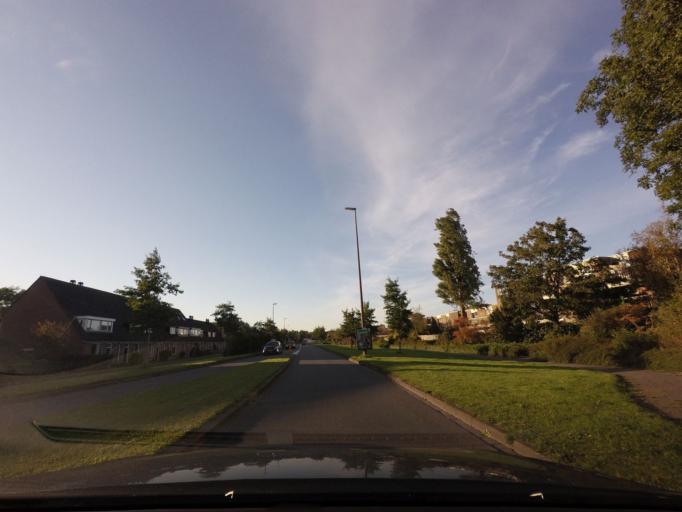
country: NL
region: North Holland
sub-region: Gemeente Alkmaar
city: Alkmaar
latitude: 52.6488
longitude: 4.7480
